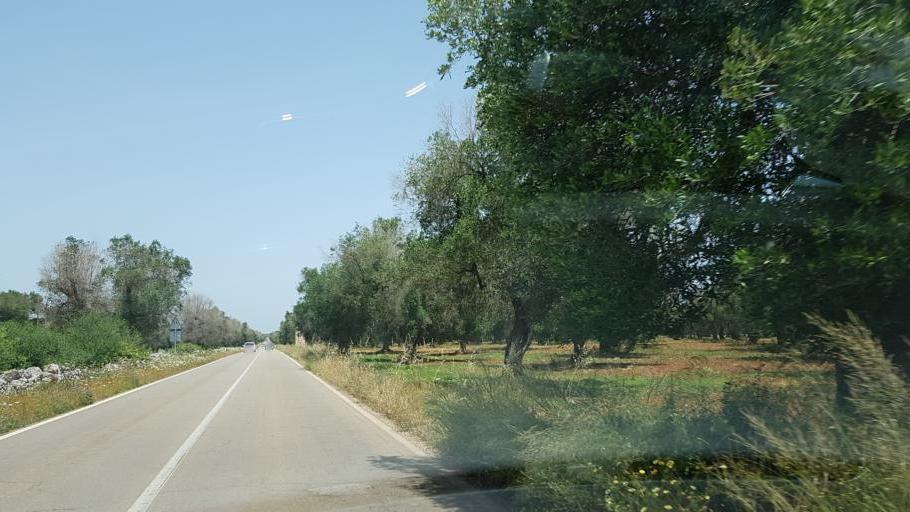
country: IT
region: Apulia
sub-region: Provincia di Lecce
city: Veglie
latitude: 40.3091
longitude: 17.9198
